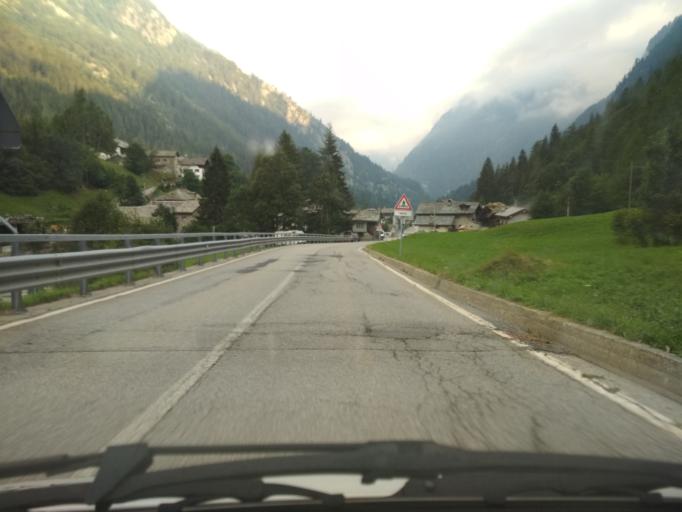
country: IT
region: Aosta Valley
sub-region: Valle d'Aosta
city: Gressoney-Saint-Jean
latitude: 45.7509
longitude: 7.8426
